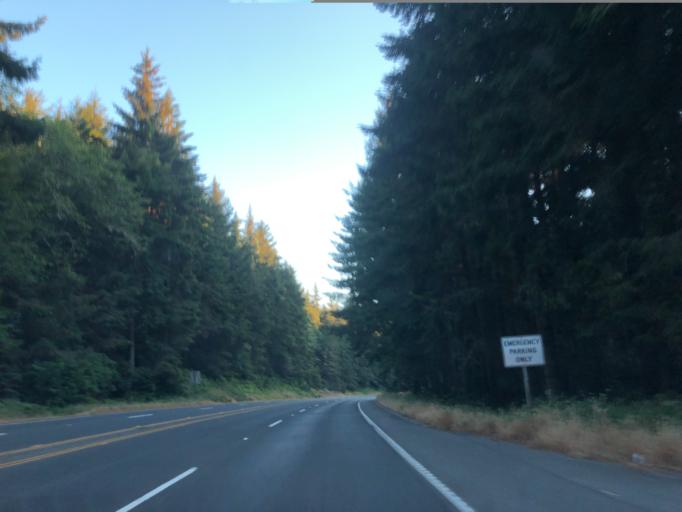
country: US
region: California
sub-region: Humboldt County
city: Westhaven-Moonstone
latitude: 41.1403
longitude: -124.1383
